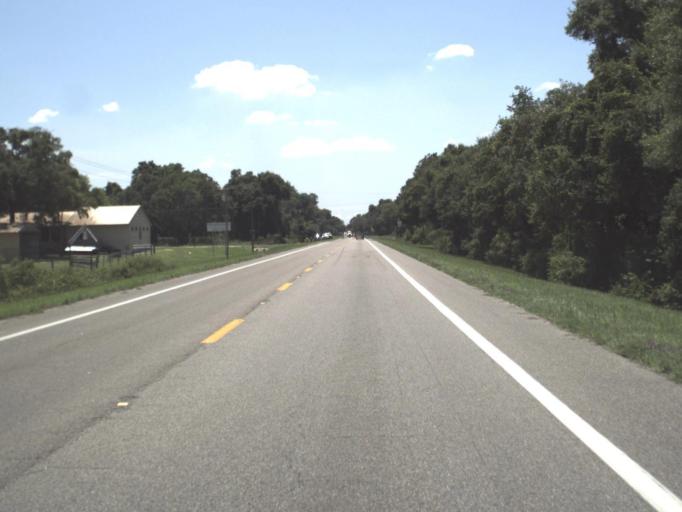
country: US
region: Florida
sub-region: Lafayette County
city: Mayo
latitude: 30.0531
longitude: -83.1569
